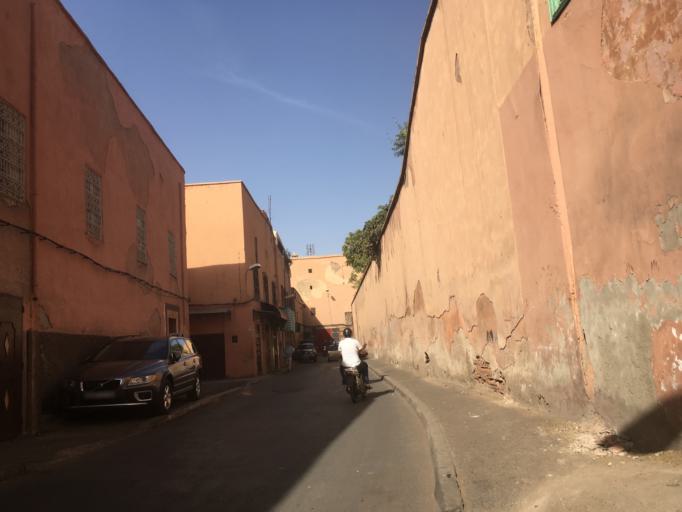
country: MA
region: Marrakech-Tensift-Al Haouz
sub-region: Marrakech
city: Marrakesh
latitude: 31.6211
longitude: -7.9821
